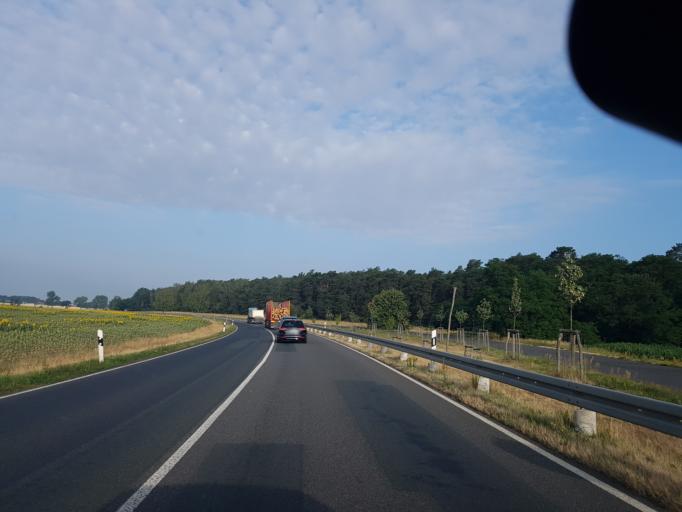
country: DE
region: Brandenburg
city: Schlieben
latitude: 51.7343
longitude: 13.3404
